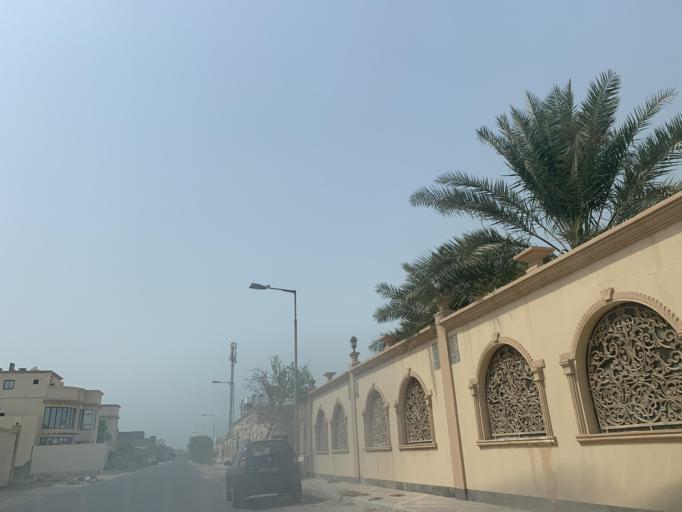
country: BH
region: Manama
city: Jidd Hafs
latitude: 26.2020
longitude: 50.4640
